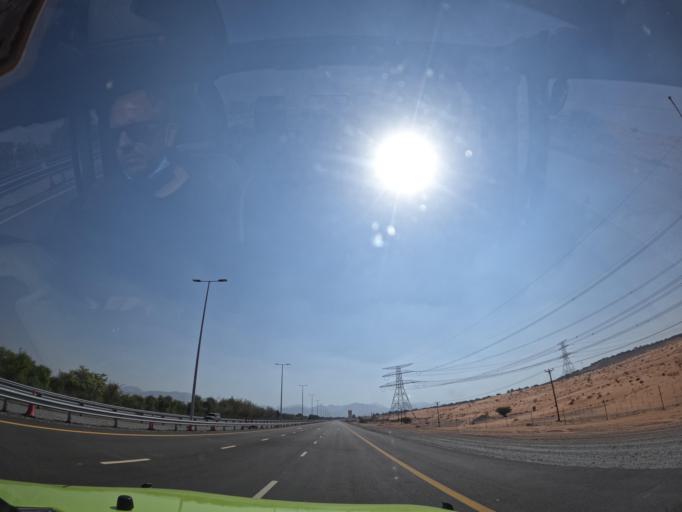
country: AE
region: Ash Shariqah
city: Adh Dhayd
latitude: 24.7932
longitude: 55.8084
